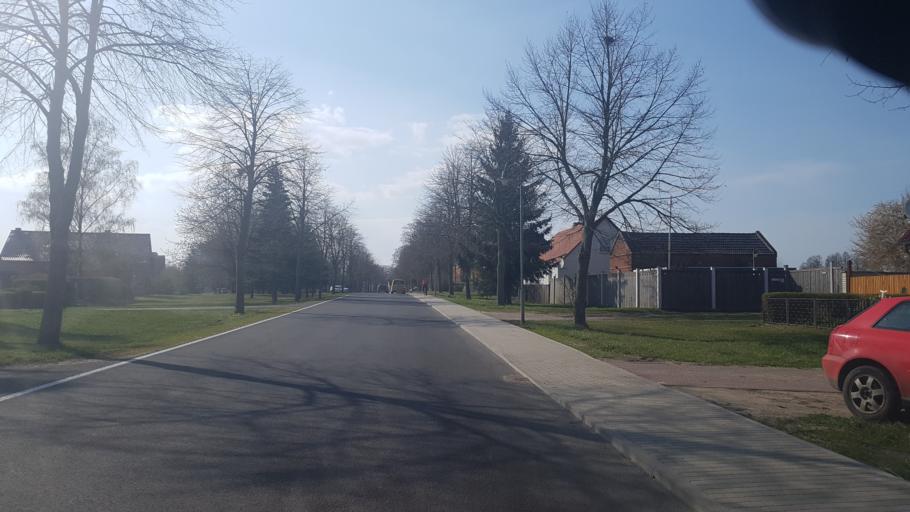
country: DE
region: Brandenburg
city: Gerswalde
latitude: 53.1612
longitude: 13.8183
